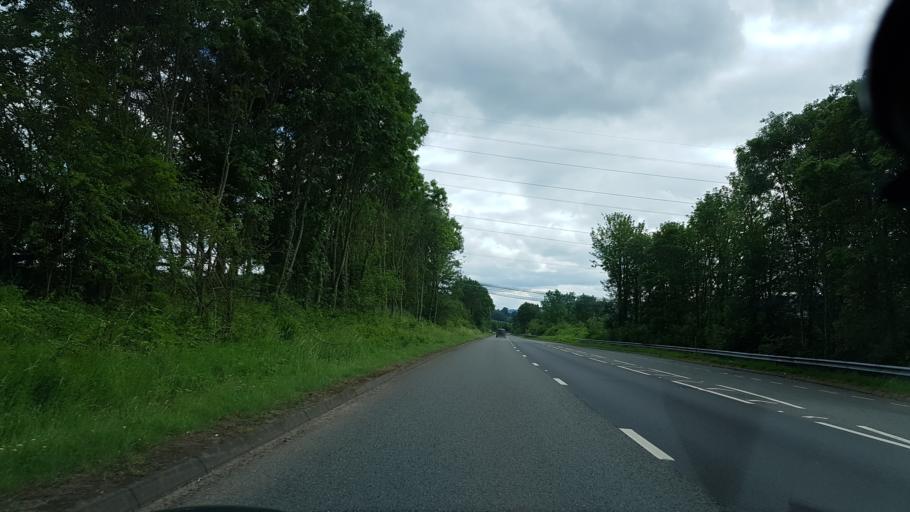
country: GB
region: Wales
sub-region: Monmouthshire
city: Abergavenny
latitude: 51.8402
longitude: -2.9994
